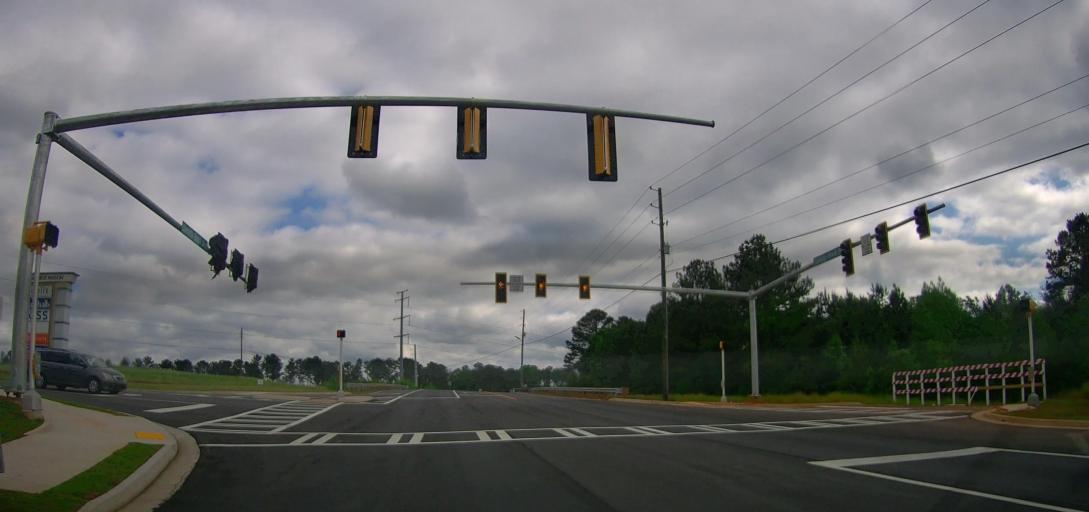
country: US
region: Georgia
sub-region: Walton County
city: Monroe
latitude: 33.8065
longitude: -83.7353
